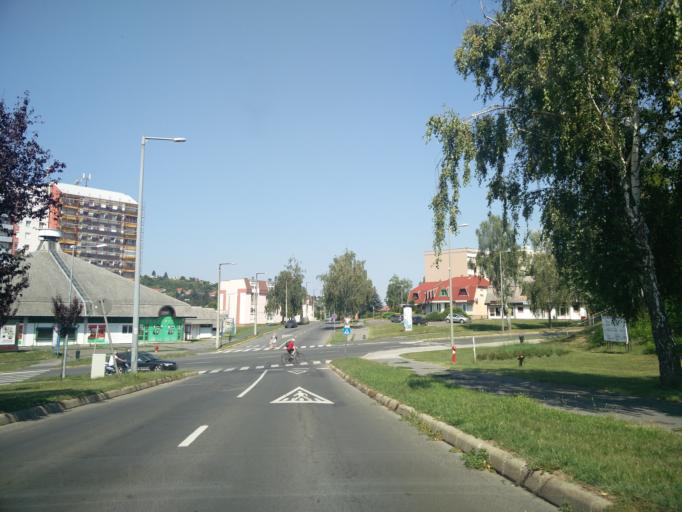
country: HU
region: Zala
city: Zalaegerszeg
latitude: 46.8248
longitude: 16.8309
